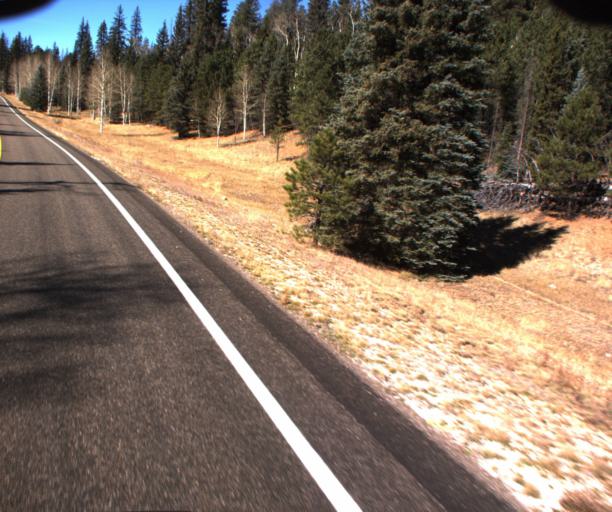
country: US
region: Arizona
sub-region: Coconino County
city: Grand Canyon
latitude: 36.5225
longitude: -112.1403
